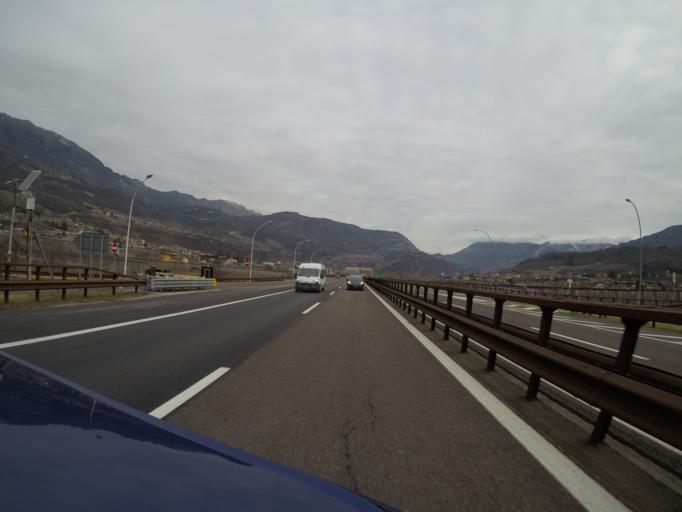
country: IT
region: Trentino-Alto Adige
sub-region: Provincia di Trento
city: Nogaredo
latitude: 45.9027
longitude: 11.0281
